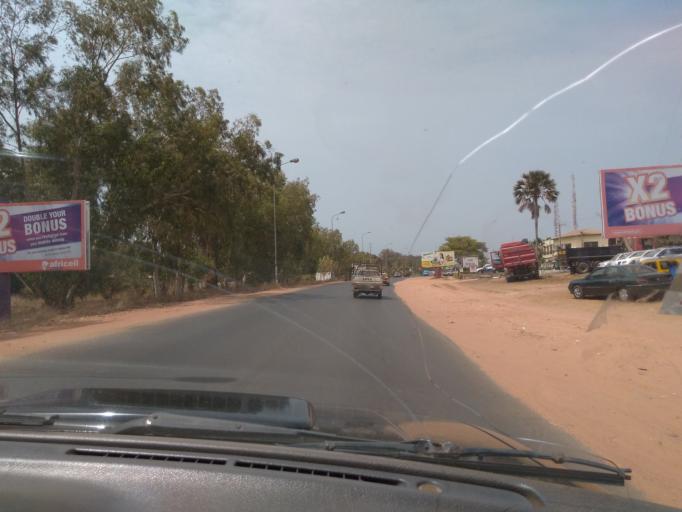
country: GM
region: Western
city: Sukuta
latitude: 13.4509
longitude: -16.7155
